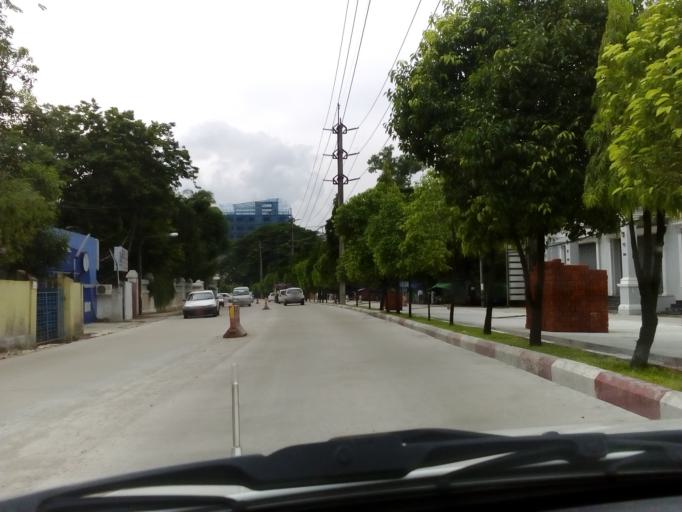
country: MM
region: Yangon
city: Yangon
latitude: 16.8657
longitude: 96.1396
